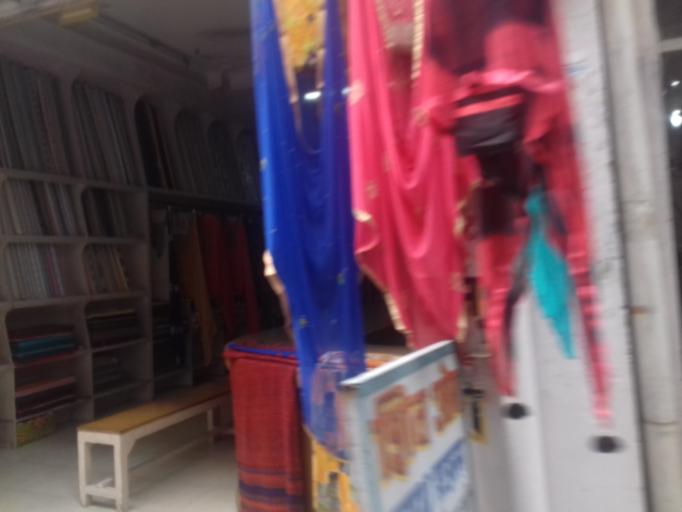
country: IN
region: Haryana
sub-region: Yamunanagar
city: Mustafabad
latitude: 30.2016
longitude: 77.1463
